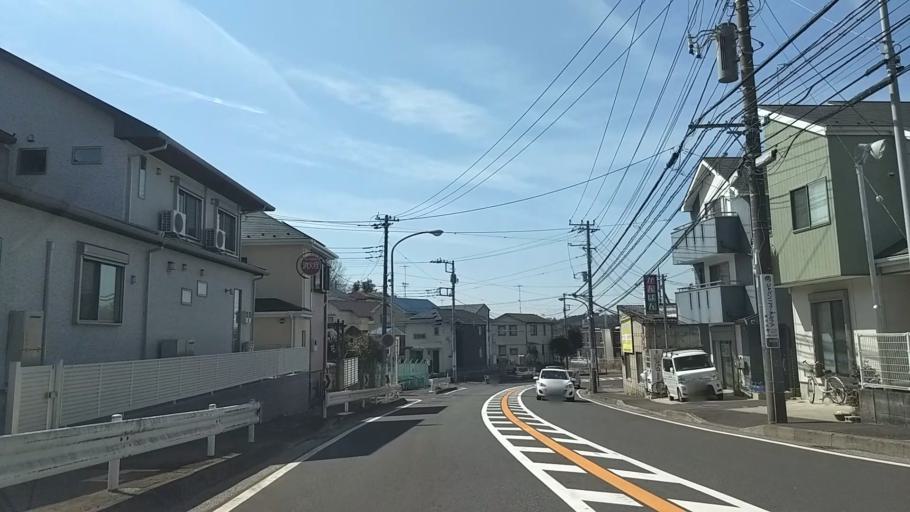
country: JP
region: Kanagawa
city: Fujisawa
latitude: 35.3824
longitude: 139.5004
